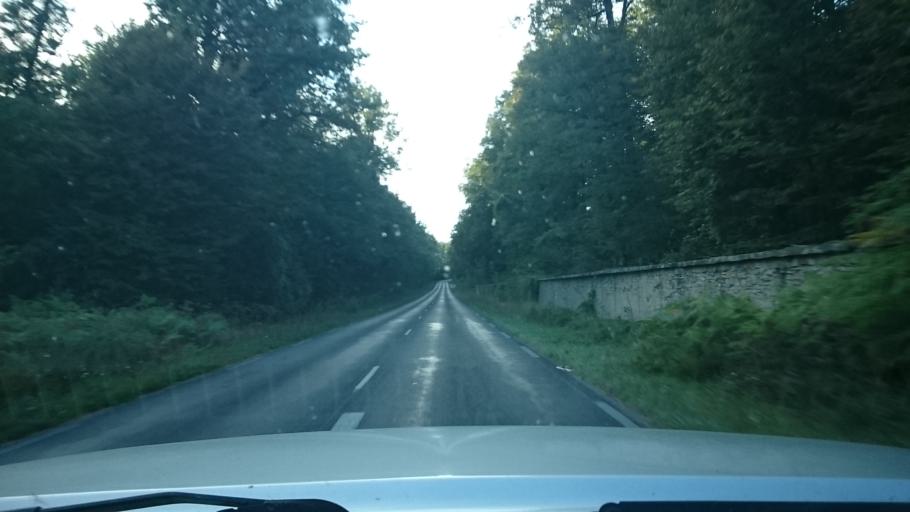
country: FR
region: Ile-de-France
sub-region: Departement de Seine-et-Marne
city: Samoreau
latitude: 48.4064
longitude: 2.7505
